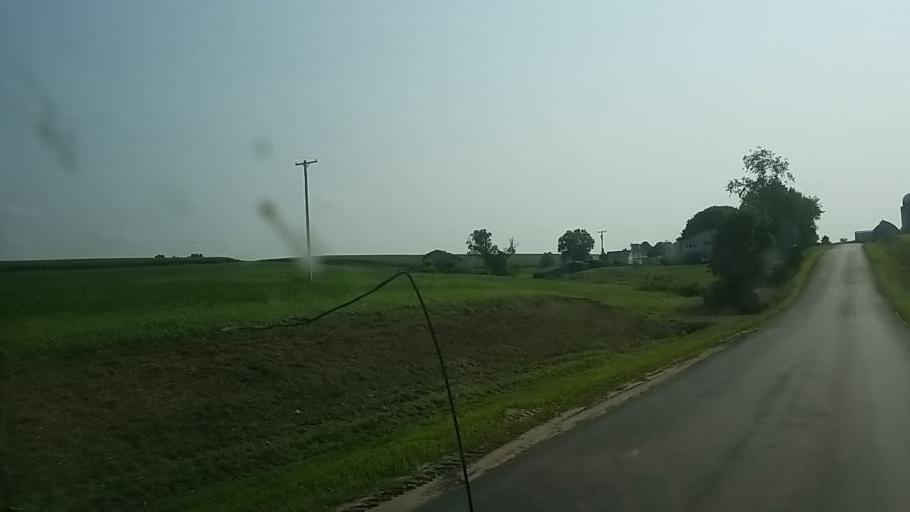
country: US
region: New York
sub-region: Montgomery County
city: Fonda
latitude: 42.9068
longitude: -74.3663
